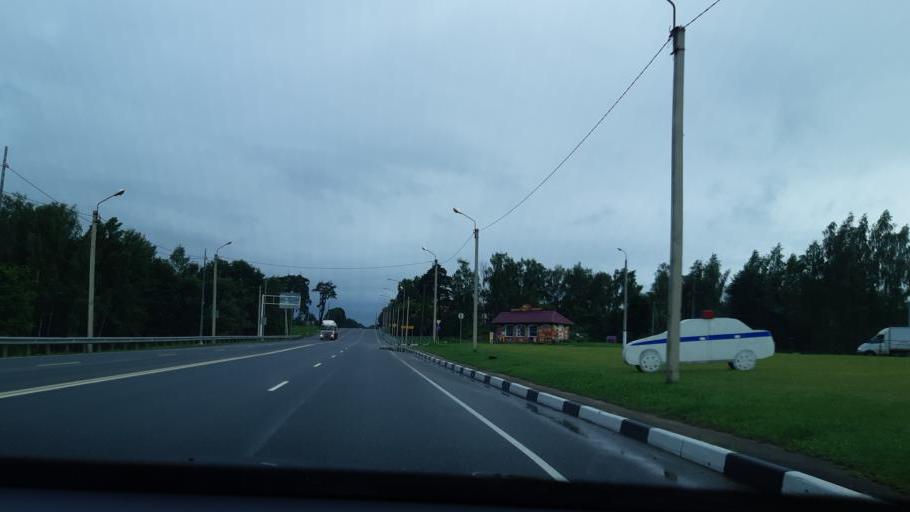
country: RU
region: Smolensk
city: Oster
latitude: 53.9857
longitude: 32.8237
